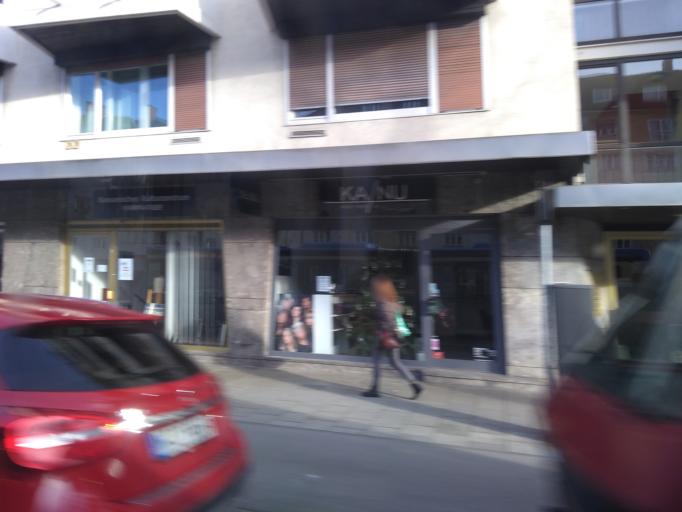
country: DE
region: Bavaria
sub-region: Upper Bavaria
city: Munich
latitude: 48.1662
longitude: 11.5864
